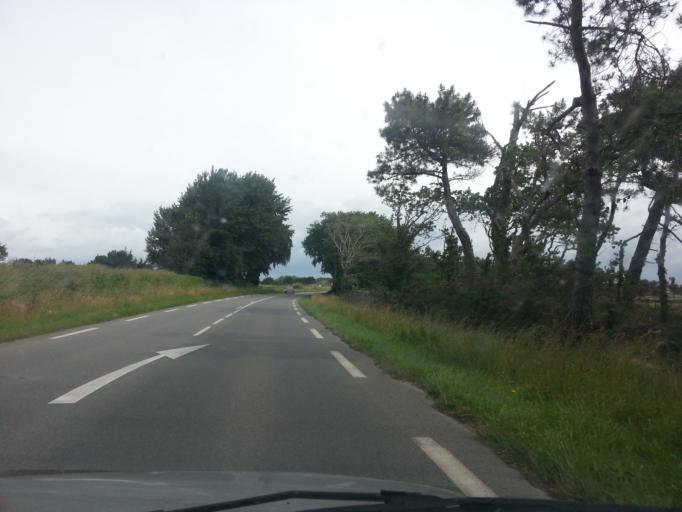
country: FR
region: Brittany
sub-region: Departement du Morbihan
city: Sainte-Helene
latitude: 47.6920
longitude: -3.2156
